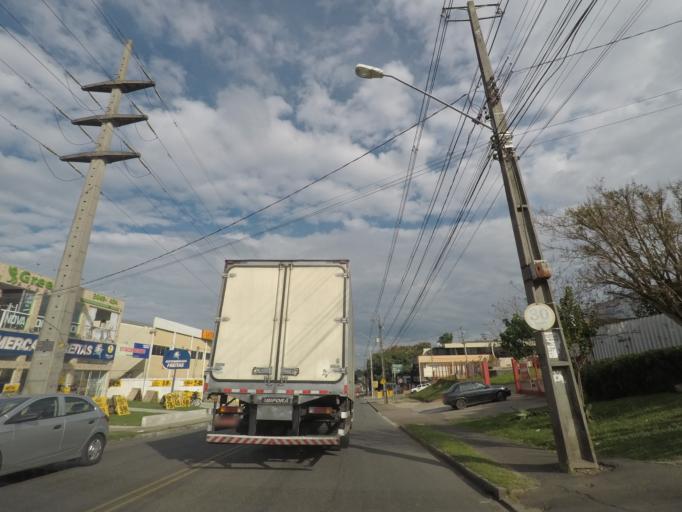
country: BR
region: Parana
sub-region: Sao Jose Dos Pinhais
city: Sao Jose dos Pinhais
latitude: -25.5498
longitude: -49.2930
